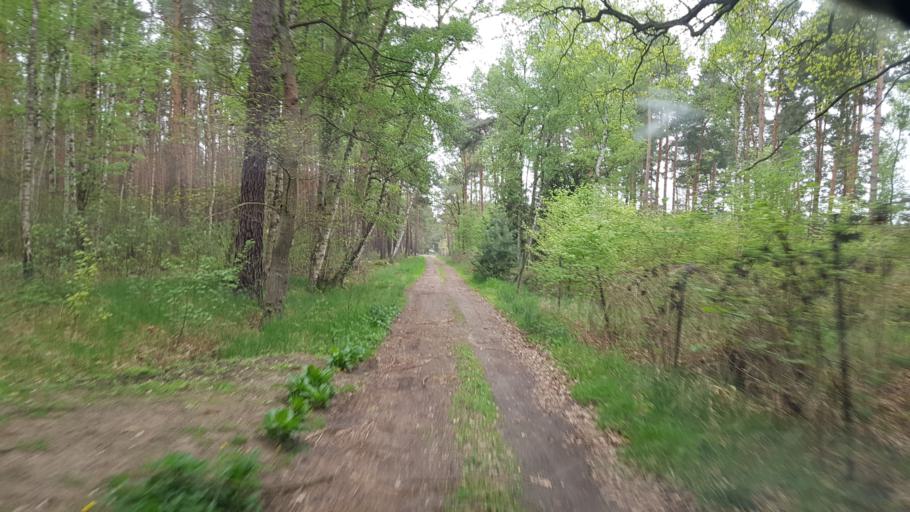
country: DE
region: Brandenburg
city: Schonewalde
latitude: 51.7100
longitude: 13.5603
